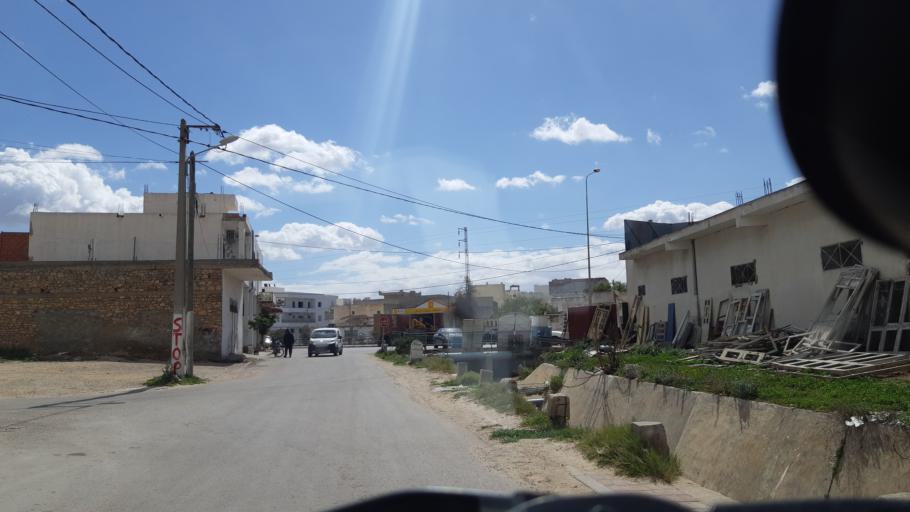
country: TN
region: Susah
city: Akouda
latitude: 35.8776
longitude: 10.5340
